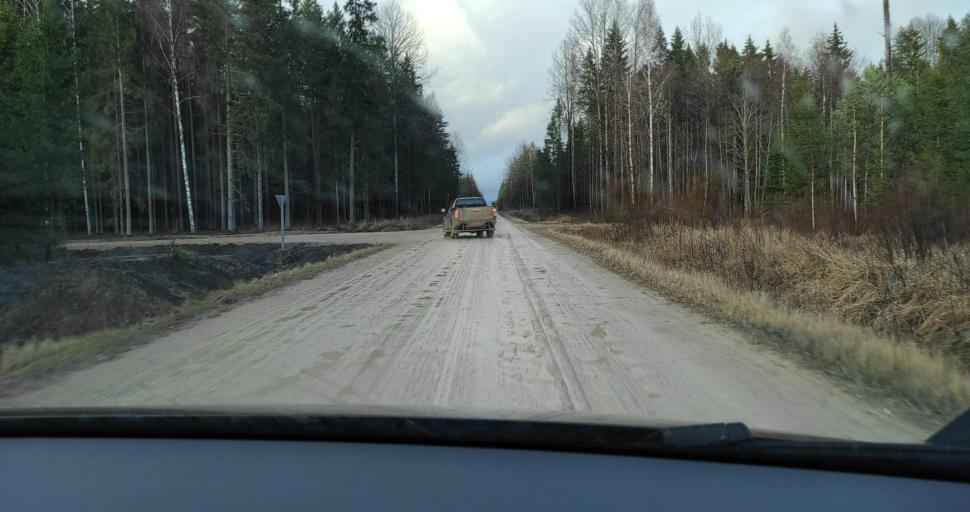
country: LV
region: Skrunda
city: Skrunda
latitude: 56.7422
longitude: 22.2055
